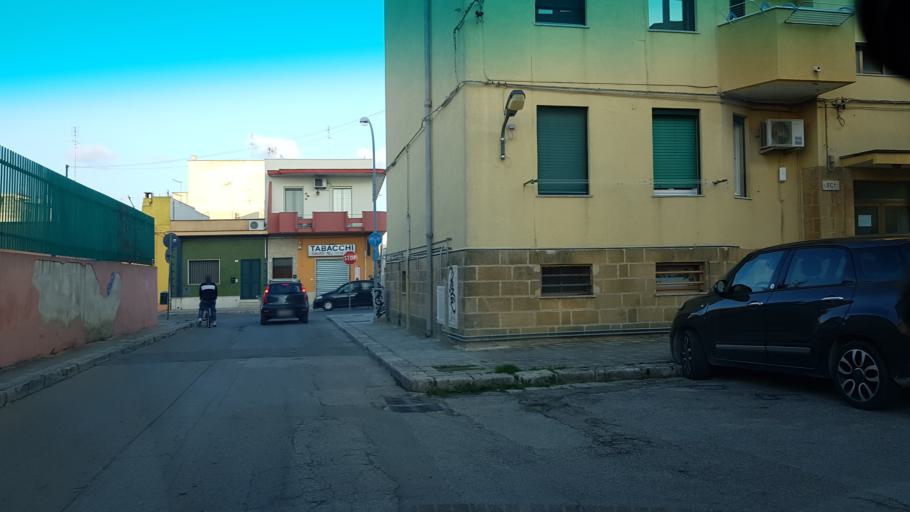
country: IT
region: Apulia
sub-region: Provincia di Brindisi
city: Mesagne
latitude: 40.5543
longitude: 17.8071
